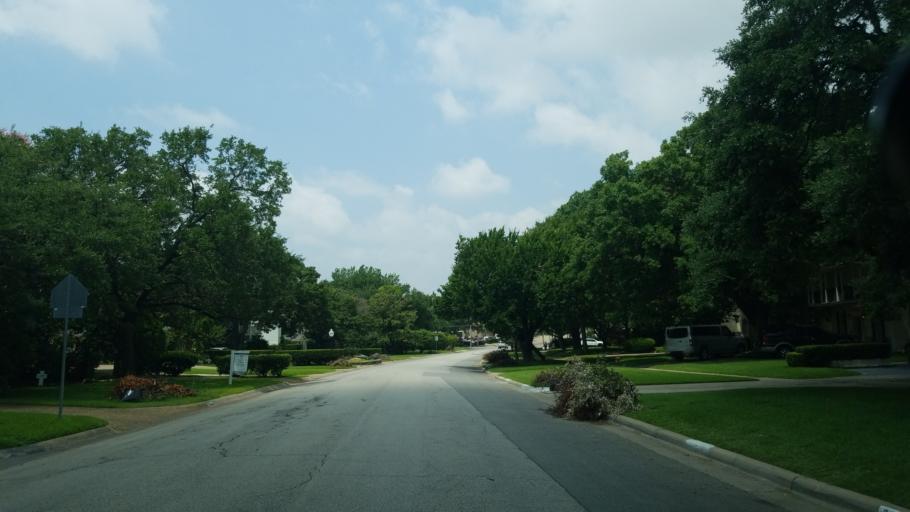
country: US
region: Texas
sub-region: Dallas County
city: University Park
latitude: 32.8452
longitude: -96.8193
